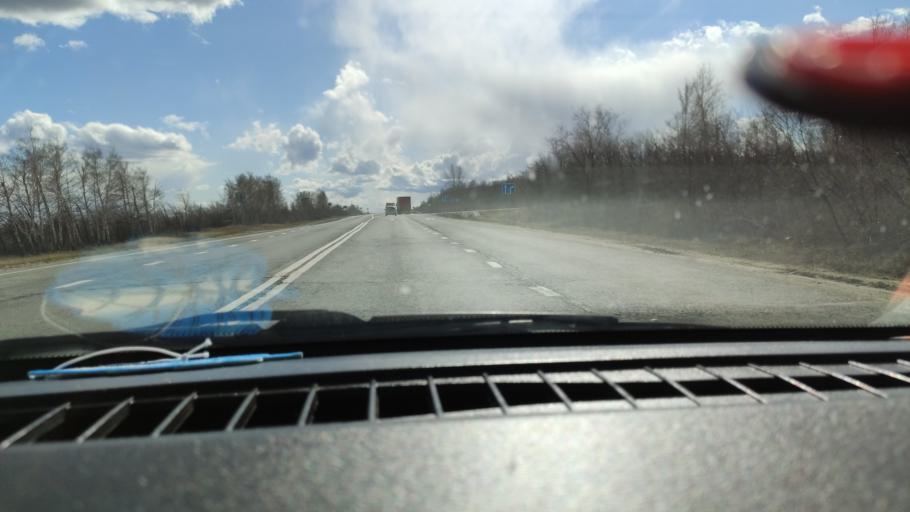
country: RU
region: Saratov
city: Dukhovnitskoye
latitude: 52.6790
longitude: 48.2307
